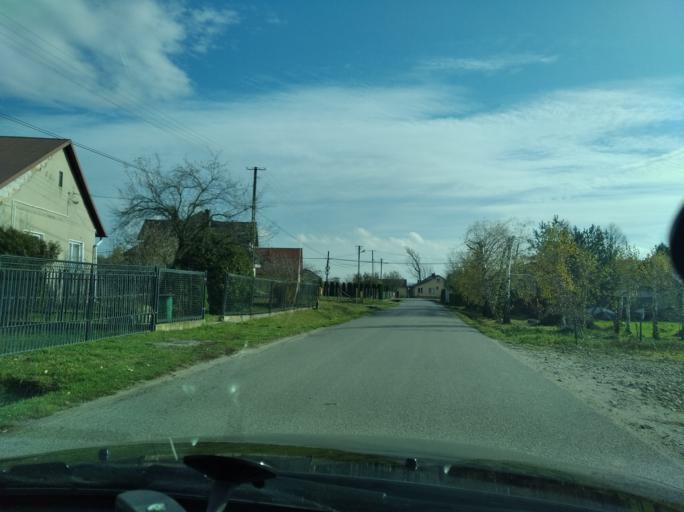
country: PL
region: Subcarpathian Voivodeship
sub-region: Powiat ropczycko-sedziszowski
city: Sedziszow Malopolski
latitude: 50.0997
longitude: 21.6641
